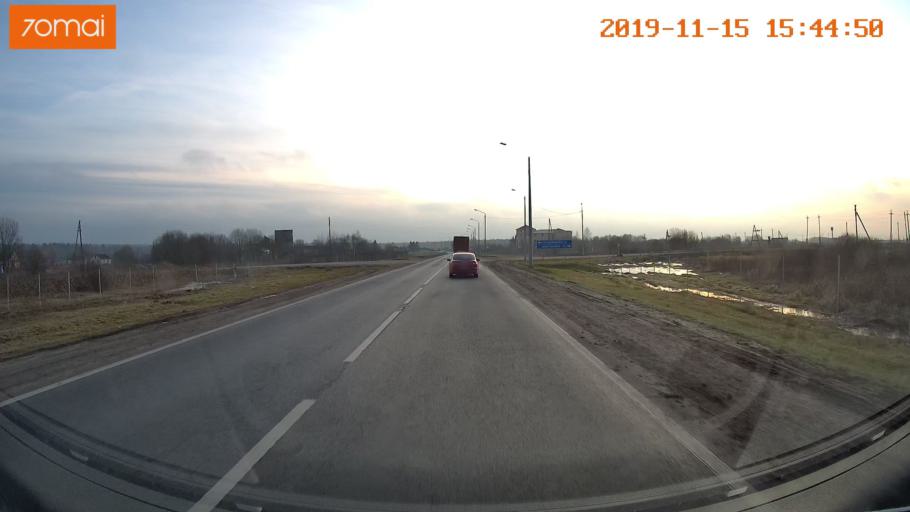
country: RU
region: Jaroslavl
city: Danilov
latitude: 57.9660
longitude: 40.0184
